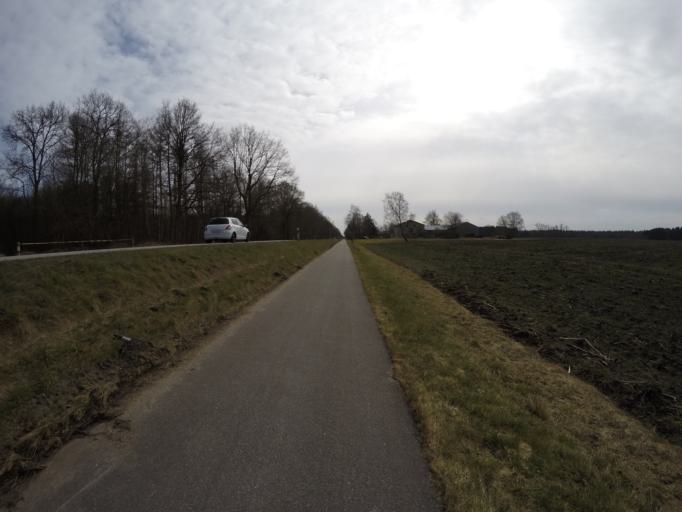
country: DE
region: Schleswig-Holstein
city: Heidmoor
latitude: 53.8306
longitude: 9.8836
